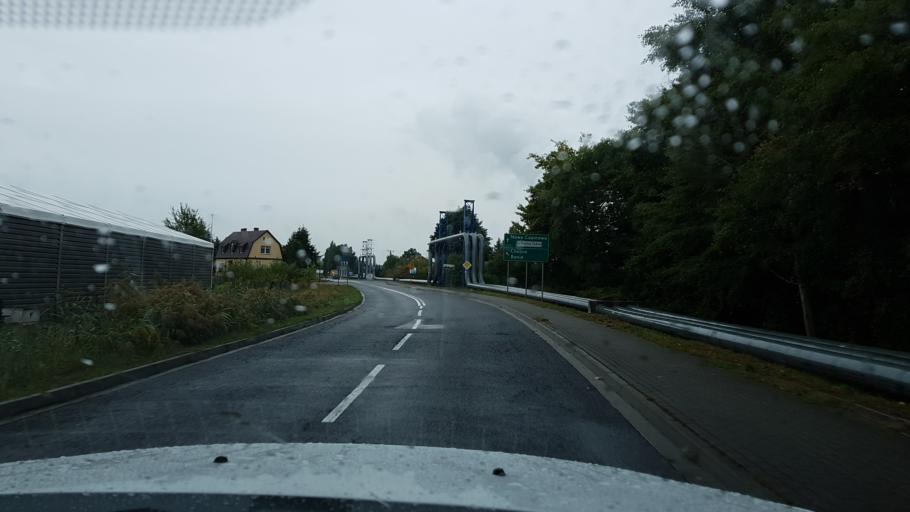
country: PL
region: West Pomeranian Voivodeship
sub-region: Powiat gryfinski
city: Gryfino
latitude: 53.2245
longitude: 14.4869
